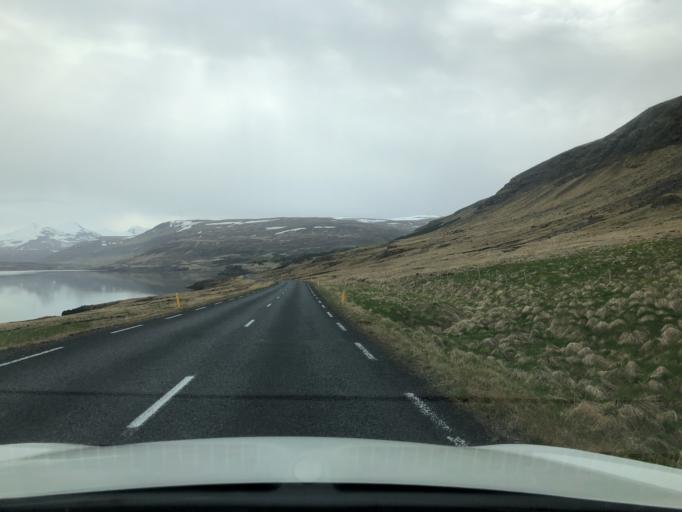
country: IS
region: Capital Region
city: Mosfellsbaer
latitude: 64.3594
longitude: -21.4993
